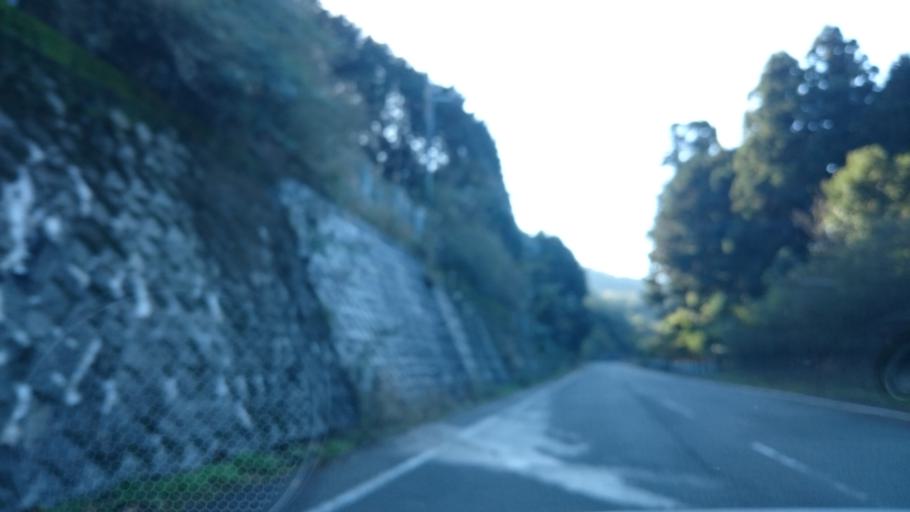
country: JP
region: Shizuoka
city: Heda
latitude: 35.0039
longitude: 138.8318
